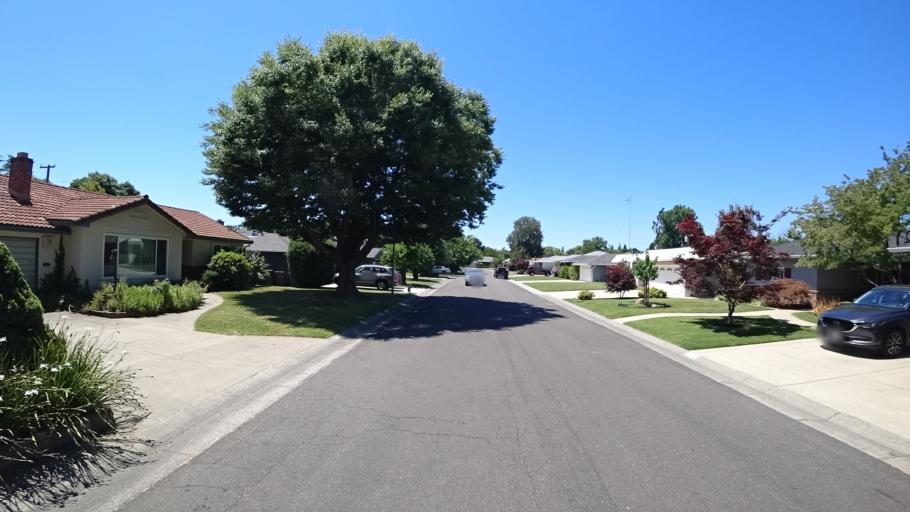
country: US
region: California
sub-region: Sacramento County
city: Sacramento
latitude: 38.5379
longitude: -121.5086
